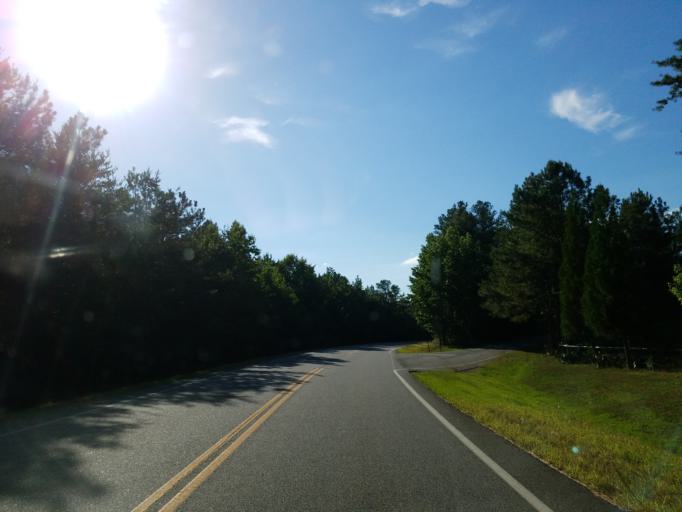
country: US
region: Georgia
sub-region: Gordon County
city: Calhoun
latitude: 34.5797
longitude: -84.9977
